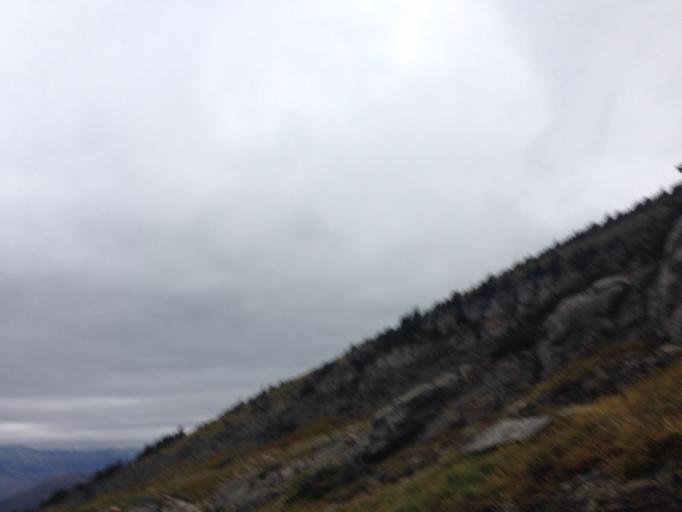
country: US
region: Montana
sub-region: Flathead County
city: Columbia Falls
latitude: 48.7445
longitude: -113.7384
